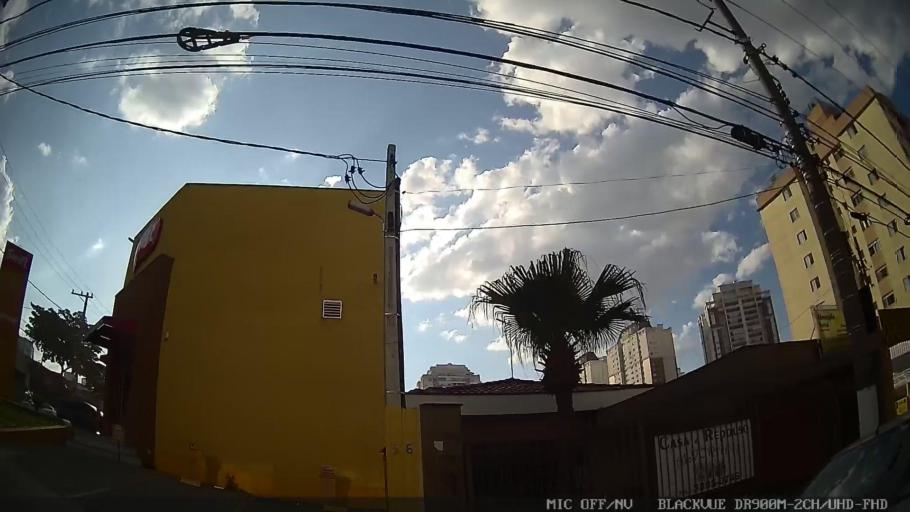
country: BR
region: Sao Paulo
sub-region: Sao Caetano Do Sul
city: Sao Caetano do Sul
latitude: -23.5475
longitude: -46.5496
